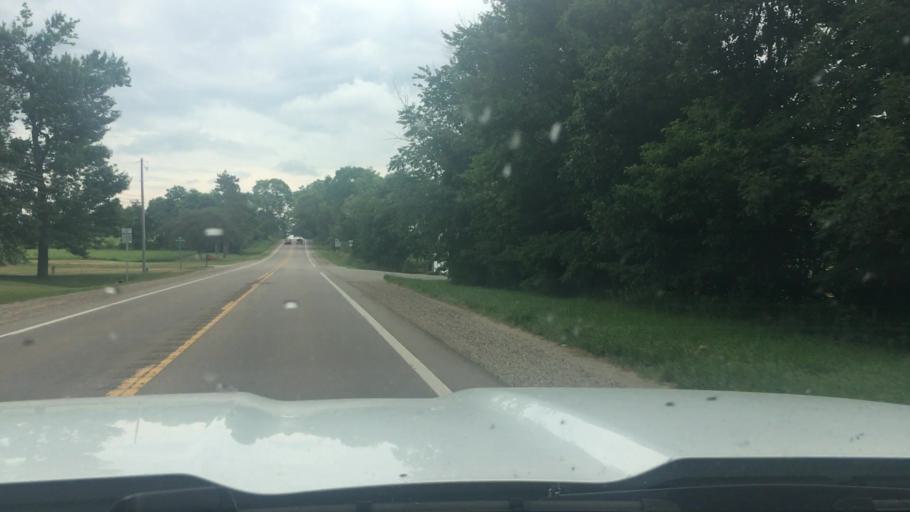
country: US
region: Michigan
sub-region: Ionia County
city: Ionia
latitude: 43.0018
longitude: -84.9748
